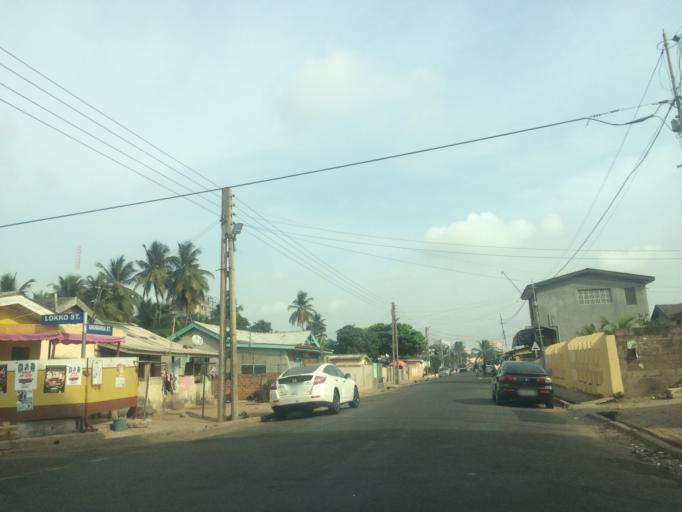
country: GH
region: Greater Accra
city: Accra
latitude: 5.5554
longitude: -0.1765
